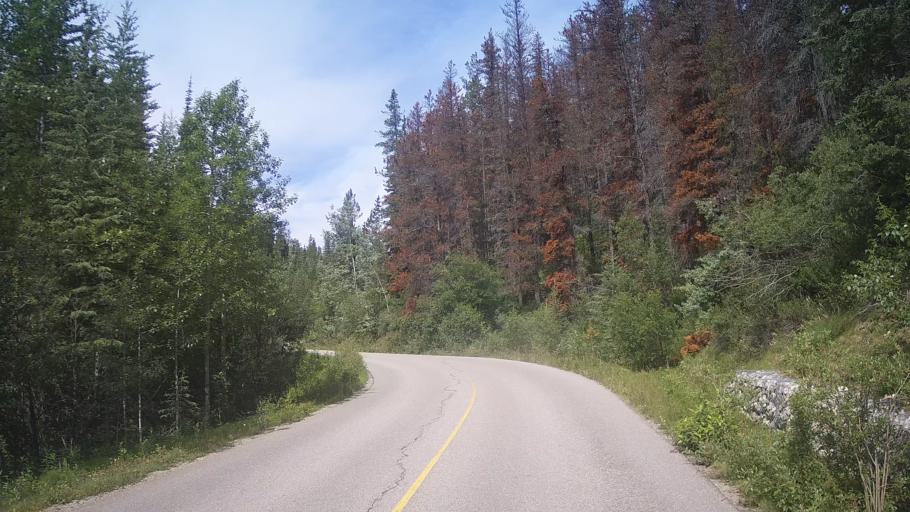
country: CA
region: Alberta
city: Hinton
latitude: 53.1770
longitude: -117.8573
